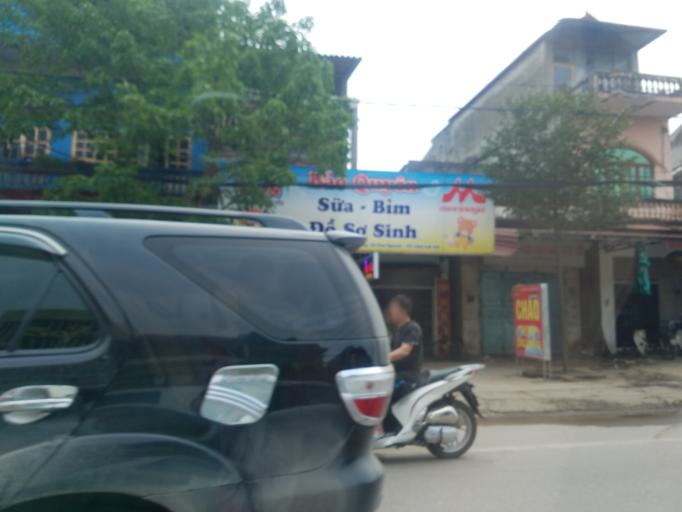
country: VN
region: Thai Nguyen
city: Chua Hang
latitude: 21.6214
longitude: 105.8411
